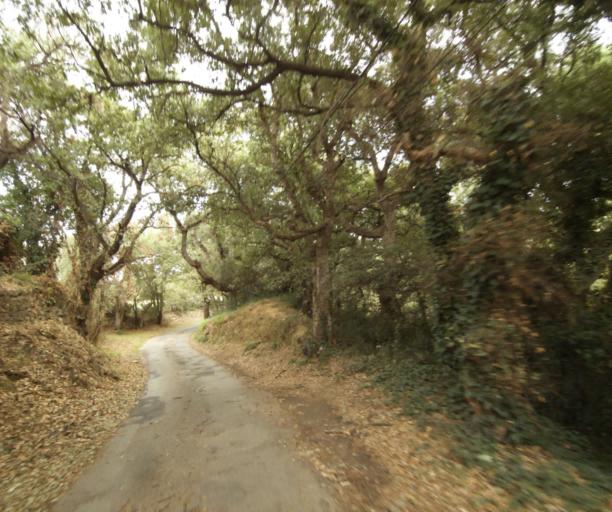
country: FR
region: Languedoc-Roussillon
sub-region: Departement des Pyrenees-Orientales
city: Argelers
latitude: 42.5340
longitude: 3.0095
